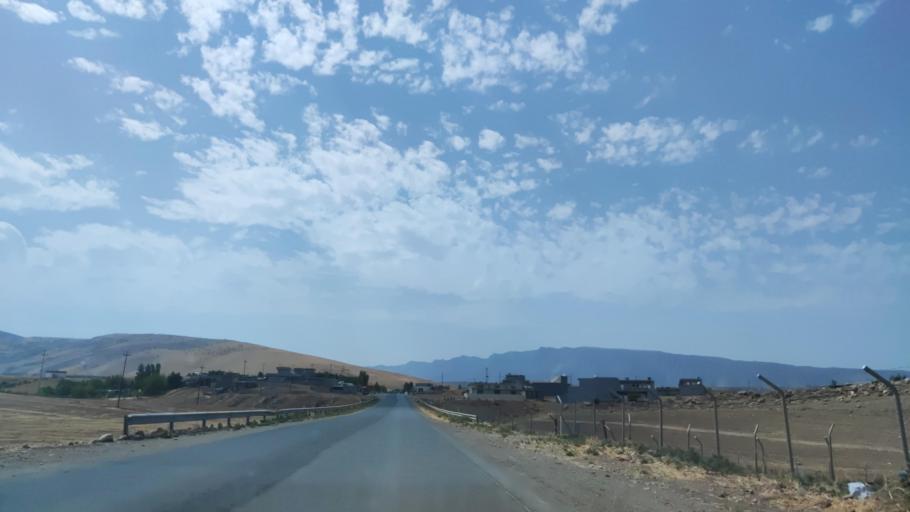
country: IQ
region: Arbil
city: Shaqlawah
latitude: 36.4812
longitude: 44.3978
